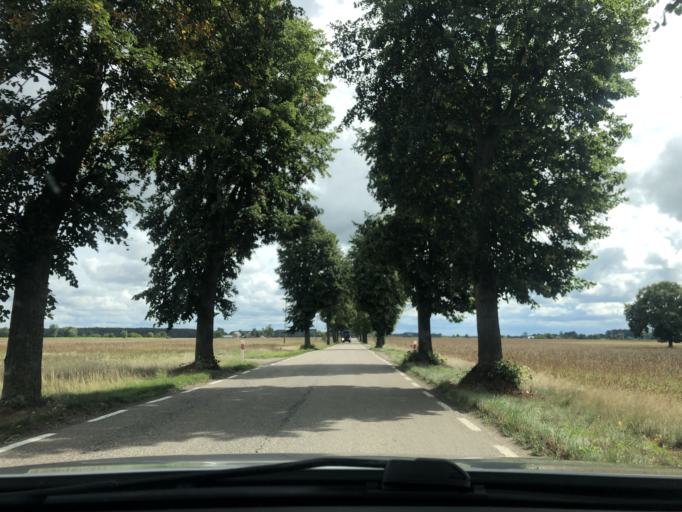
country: PL
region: Greater Poland Voivodeship
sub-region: Powiat czarnkowsko-trzcianecki
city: Krzyz Wielkopolski
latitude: 52.9128
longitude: 16.0621
